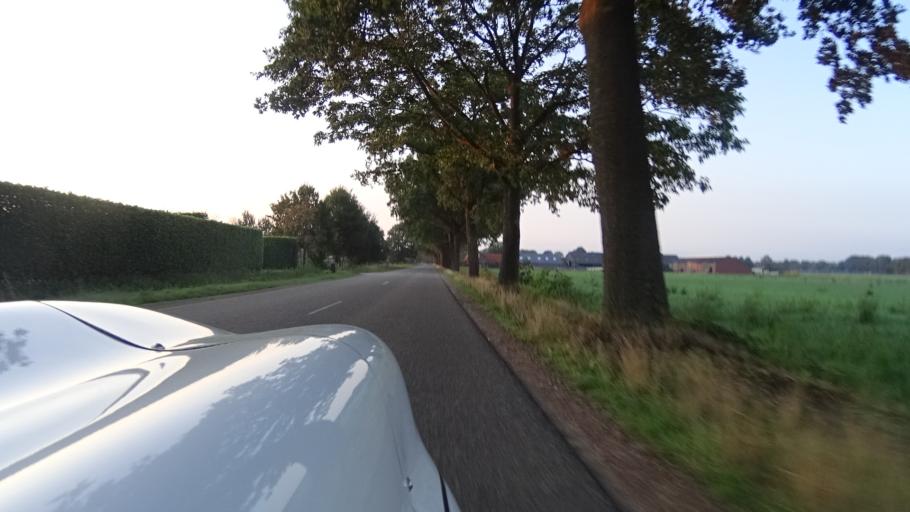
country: NL
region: North Brabant
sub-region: Gemeente Mill en Sint Hubert
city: Wilbertoord
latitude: 51.5998
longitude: 5.7894
